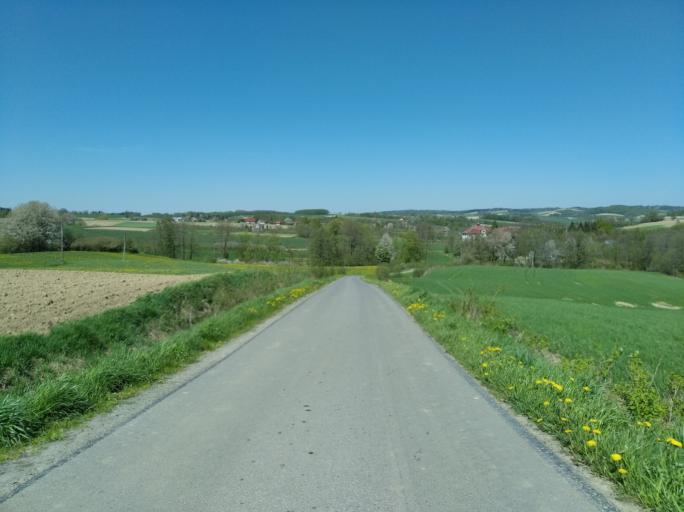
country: PL
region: Subcarpathian Voivodeship
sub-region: Powiat ropczycko-sedziszowski
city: Wielopole Skrzynskie
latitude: 49.9130
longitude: 21.5494
